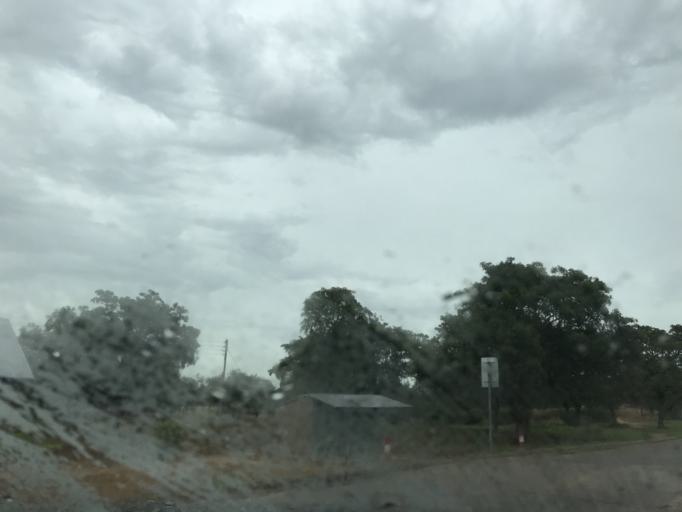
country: GH
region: Upper West
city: Wa
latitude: 10.5135
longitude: -2.6961
